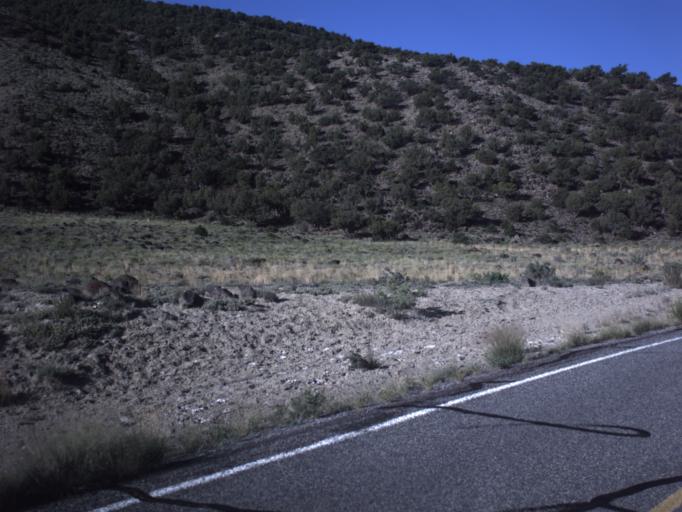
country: US
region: Utah
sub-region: Emery County
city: Ferron
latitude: 38.7642
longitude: -111.3550
